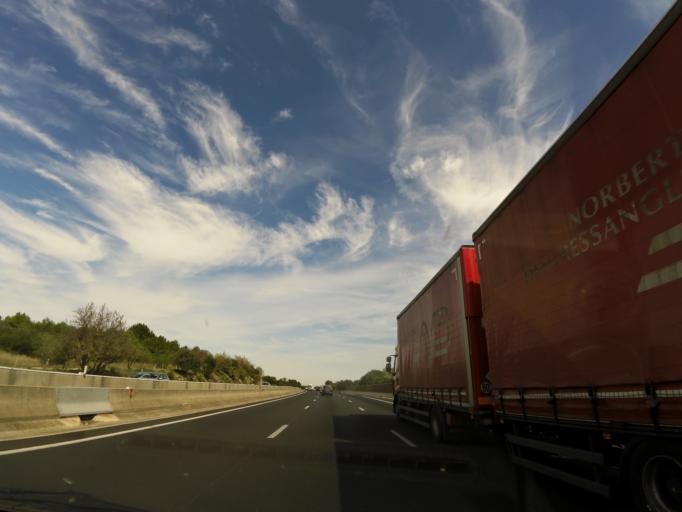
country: FR
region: Languedoc-Roussillon
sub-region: Departement du Gard
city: Uchaud
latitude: 43.7609
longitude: 4.2643
